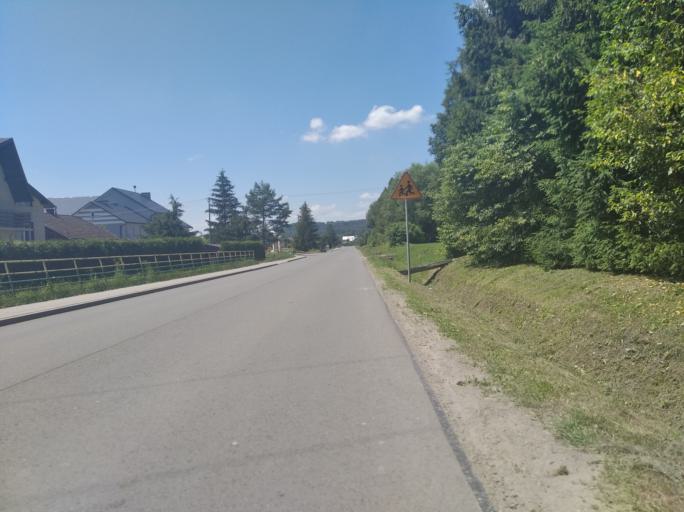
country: PL
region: Subcarpathian Voivodeship
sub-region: Powiat brzozowski
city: Niebocko
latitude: 49.6781
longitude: 22.1099
